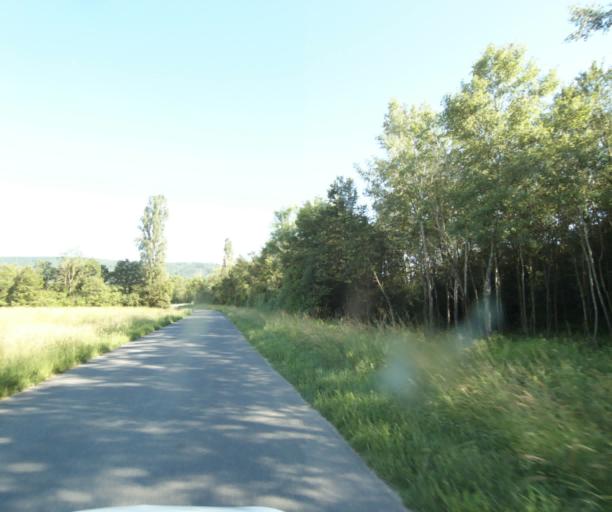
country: FR
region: Rhone-Alpes
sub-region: Departement de la Haute-Savoie
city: Massongy
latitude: 46.3313
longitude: 6.3288
